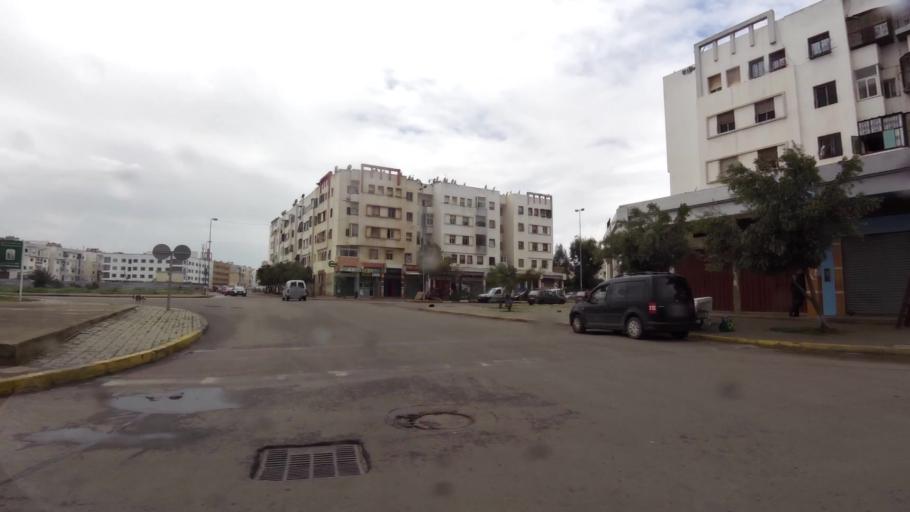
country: MA
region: Grand Casablanca
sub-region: Casablanca
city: Casablanca
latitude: 33.5447
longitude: -7.6853
